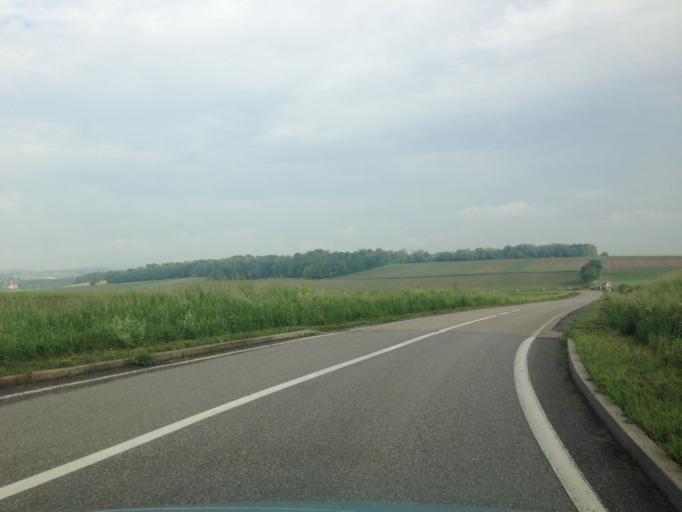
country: FR
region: Alsace
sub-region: Departement du Bas-Rhin
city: Schwindratzheim
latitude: 48.7773
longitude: 7.5904
